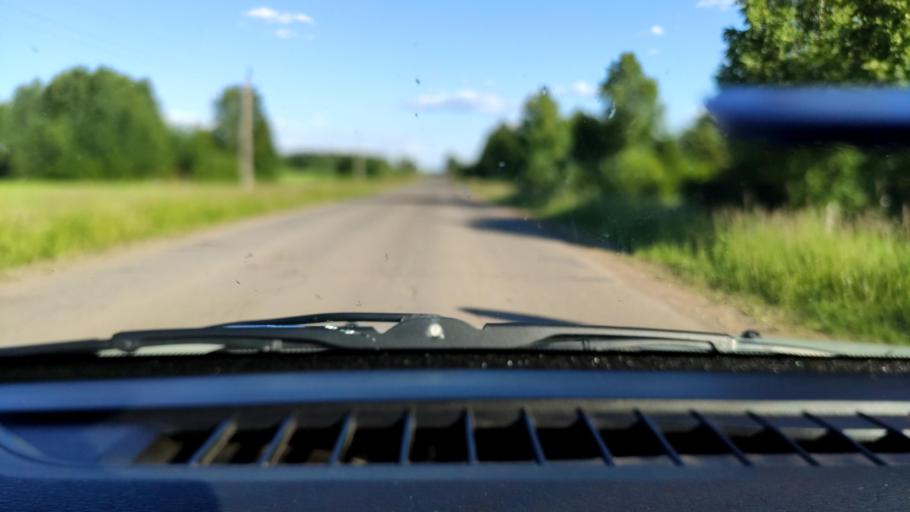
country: RU
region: Perm
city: Uinskoye
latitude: 57.0978
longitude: 56.5455
